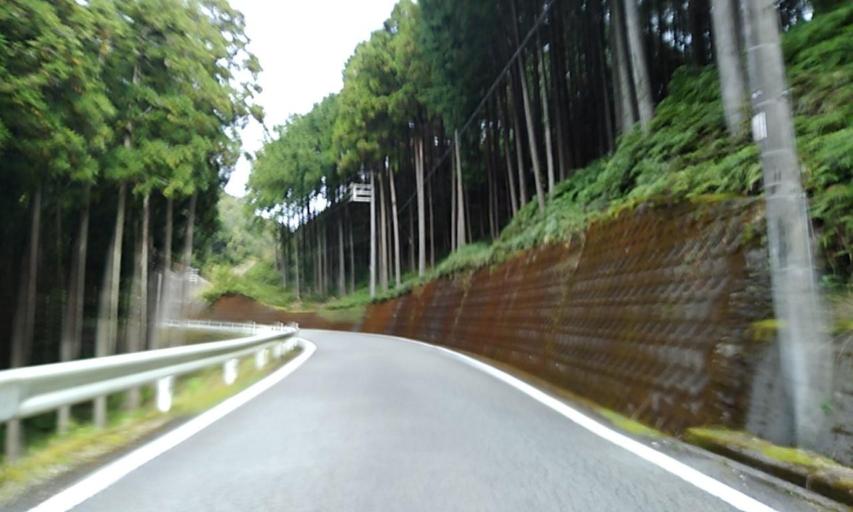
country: JP
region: Wakayama
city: Shingu
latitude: 33.5447
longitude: 135.8459
